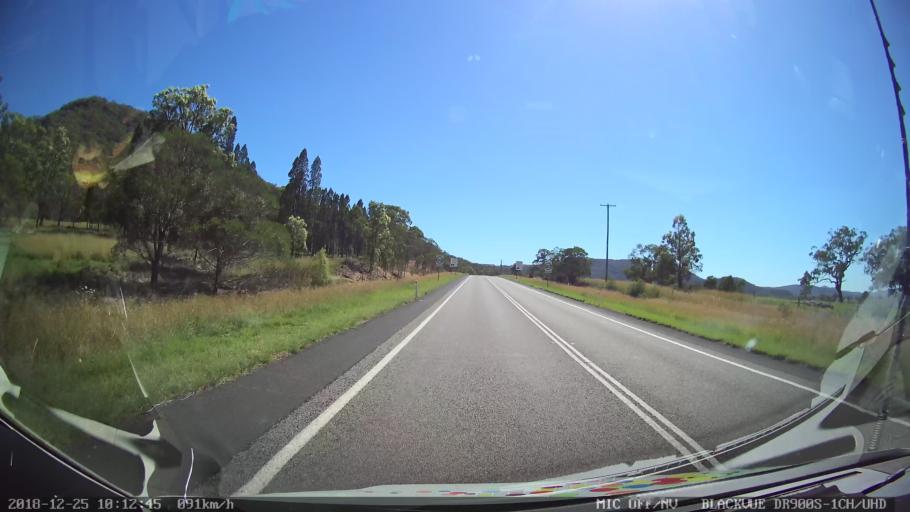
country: AU
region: New South Wales
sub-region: Muswellbrook
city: Denman
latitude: -32.3283
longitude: 150.5354
